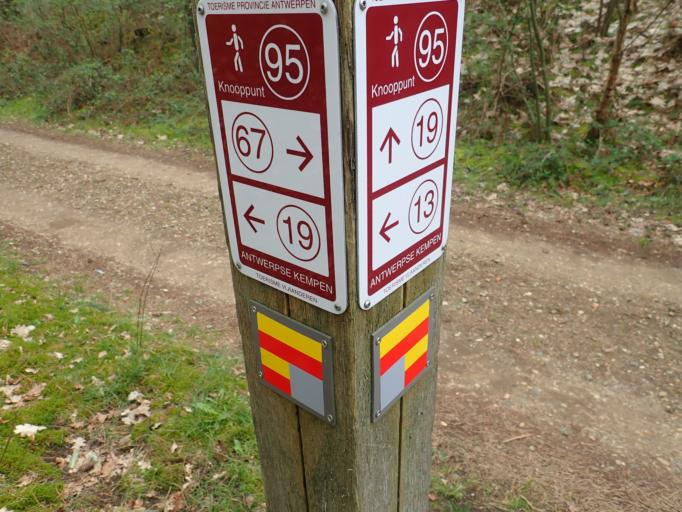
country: BE
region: Flanders
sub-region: Provincie Antwerpen
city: Herentals
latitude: 51.2016
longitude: 4.8413
